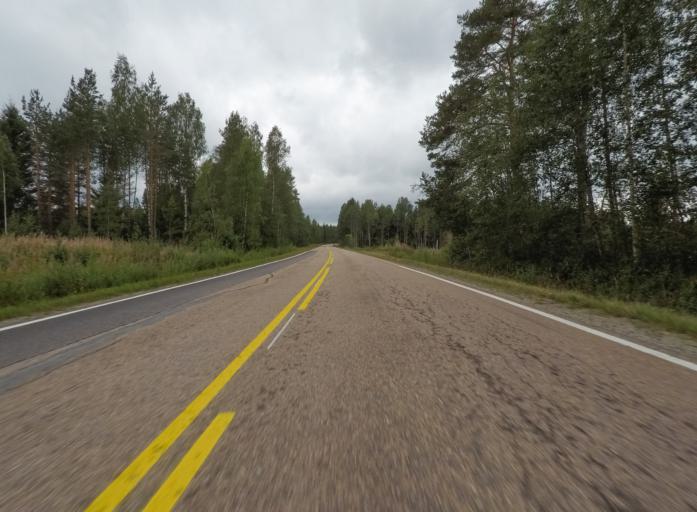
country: FI
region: Central Finland
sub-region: Jyvaeskylae
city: Hankasalmi
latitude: 62.3613
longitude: 26.5385
